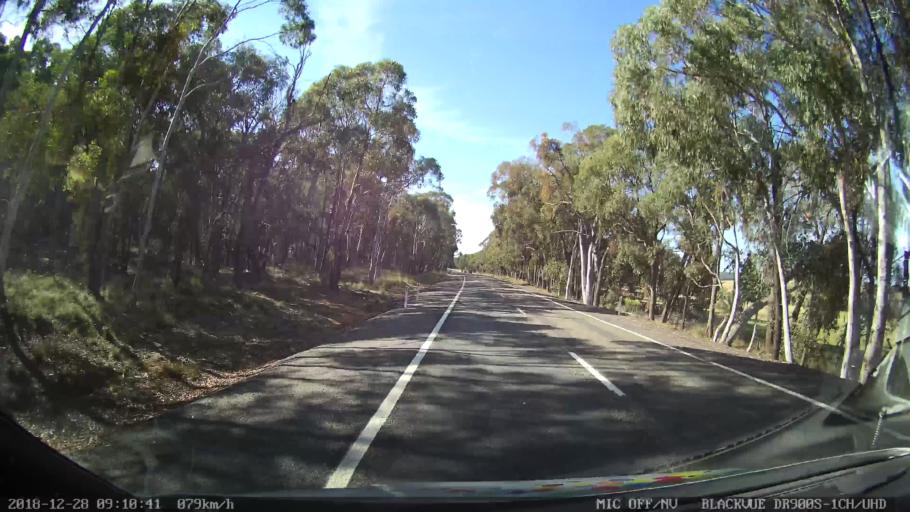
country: AU
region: New South Wales
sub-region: Upper Lachlan Shire
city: Crookwell
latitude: -34.2346
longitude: 149.3369
